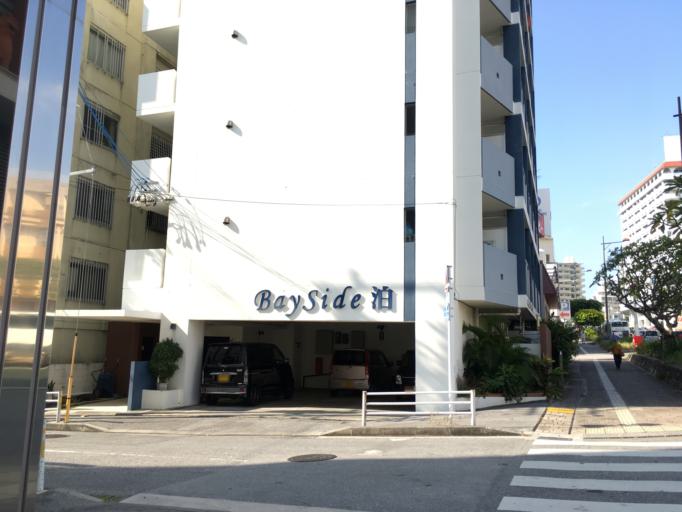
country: JP
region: Okinawa
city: Naha-shi
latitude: 26.2264
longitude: 127.6856
